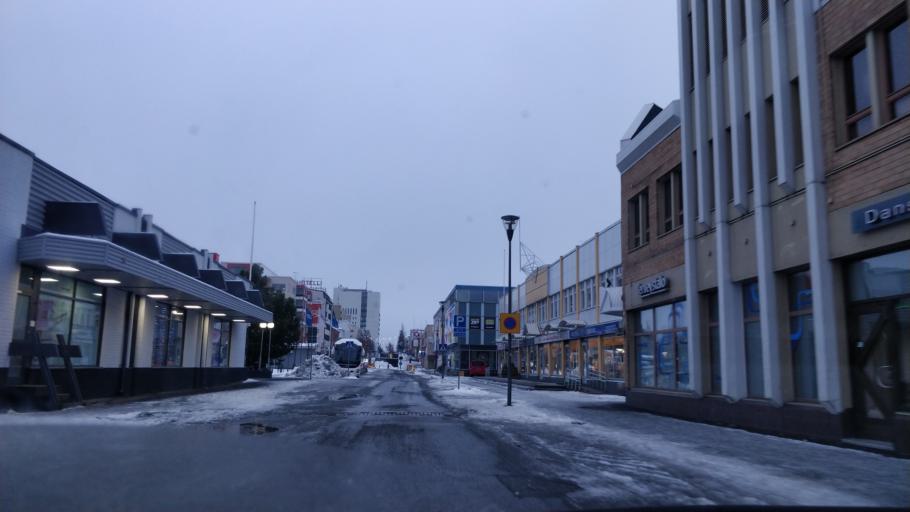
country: FI
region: Lapland
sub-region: Kemi-Tornio
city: Kemi
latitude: 65.7388
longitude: 24.5620
